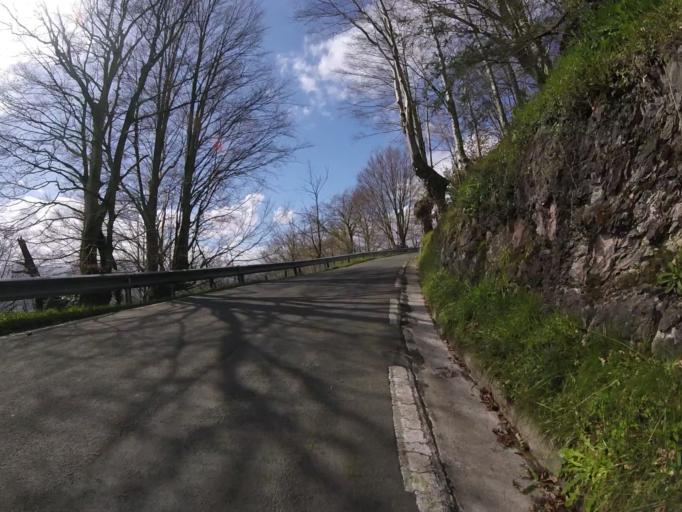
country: ES
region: Basque Country
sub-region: Provincia de Guipuzcoa
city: Tolosa
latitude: 43.1320
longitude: -2.1028
